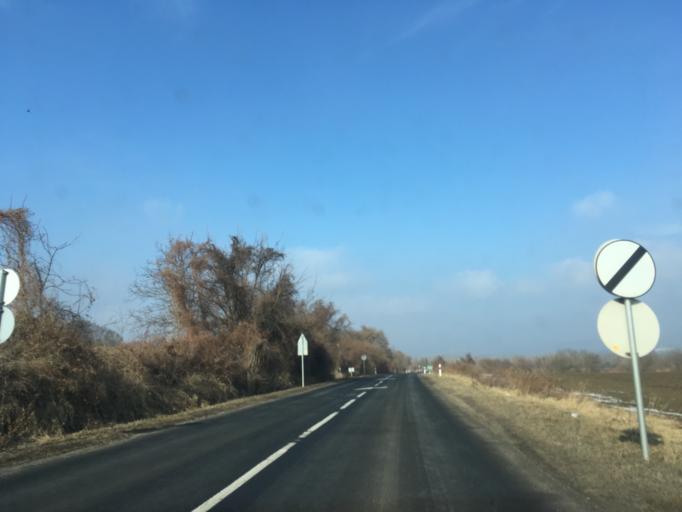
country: HU
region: Komarom-Esztergom
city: Pilismarot
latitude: 47.7919
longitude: 18.8661
